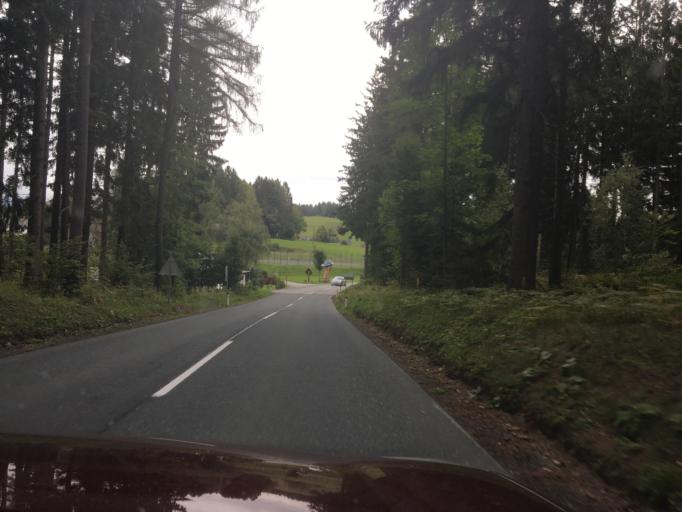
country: AT
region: Styria
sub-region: Politischer Bezirk Deutschlandsberg
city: Trahutten
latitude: 46.8199
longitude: 15.1576
